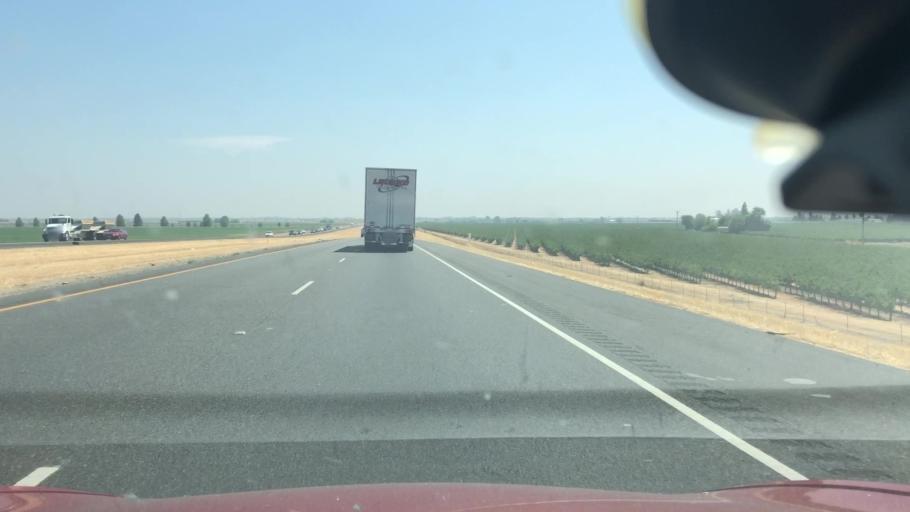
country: US
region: California
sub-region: Sacramento County
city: Walnut Grove
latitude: 38.3187
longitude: -121.4653
